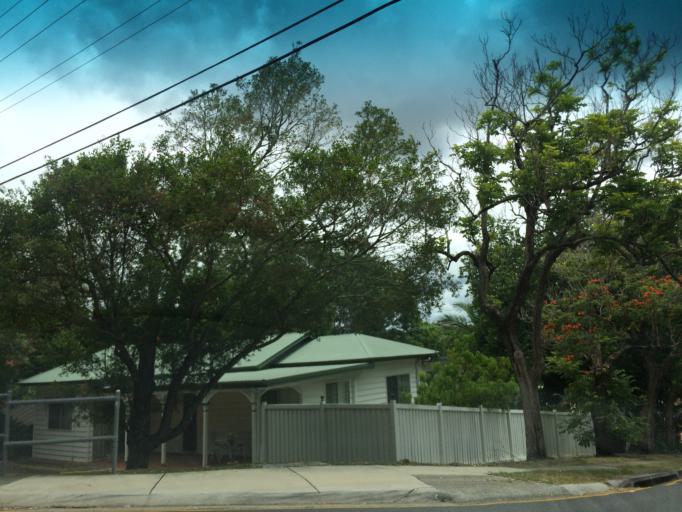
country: AU
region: Queensland
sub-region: Brisbane
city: Kenmore Hills
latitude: -27.5194
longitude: 152.9459
